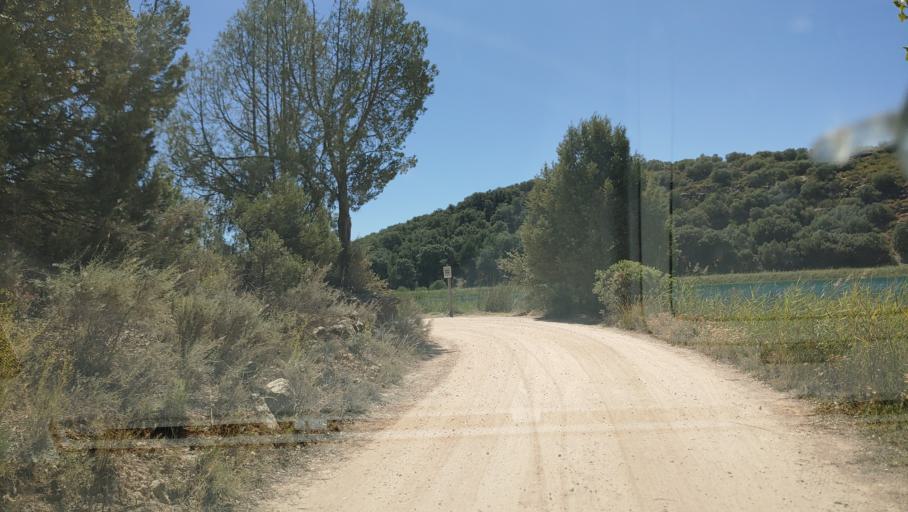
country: ES
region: Castille-La Mancha
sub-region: Provincia de Albacete
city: Ossa de Montiel
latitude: 38.9251
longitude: -2.8132
